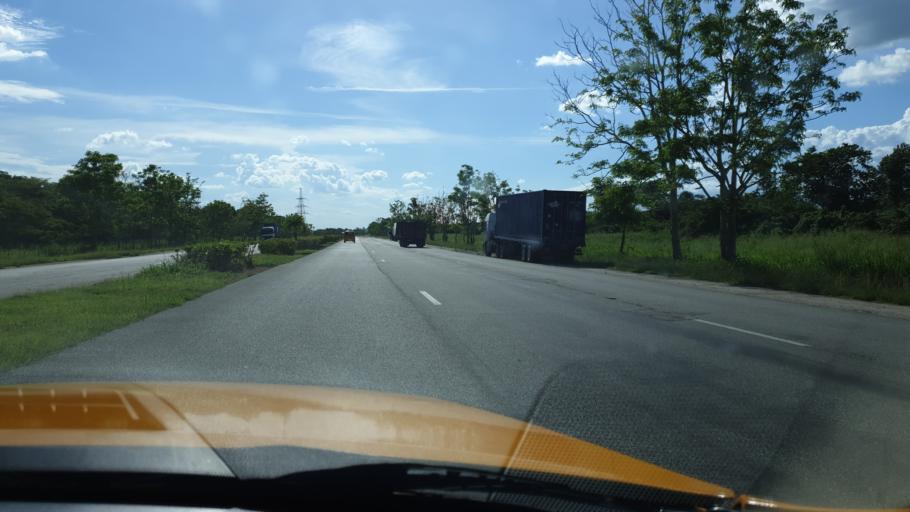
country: CU
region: Cienfuegos
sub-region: Municipio de Aguada de Pasajeros
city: Aguada de Pasajeros
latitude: 22.4078
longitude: -80.8811
